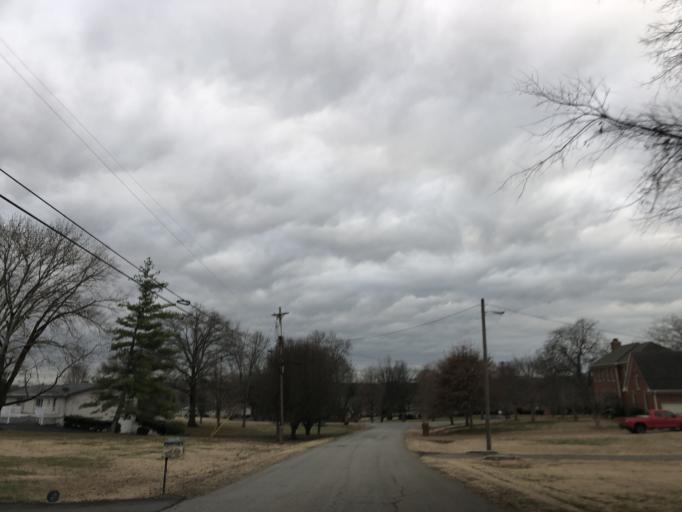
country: US
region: Tennessee
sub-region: Davidson County
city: Goodlettsville
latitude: 36.2964
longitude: -86.6846
